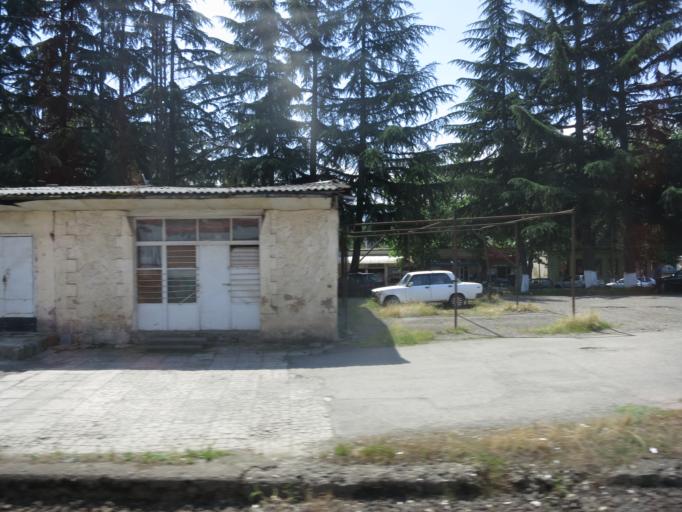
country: GE
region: Imereti
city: Zestap'oni
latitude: 42.1074
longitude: 43.0359
